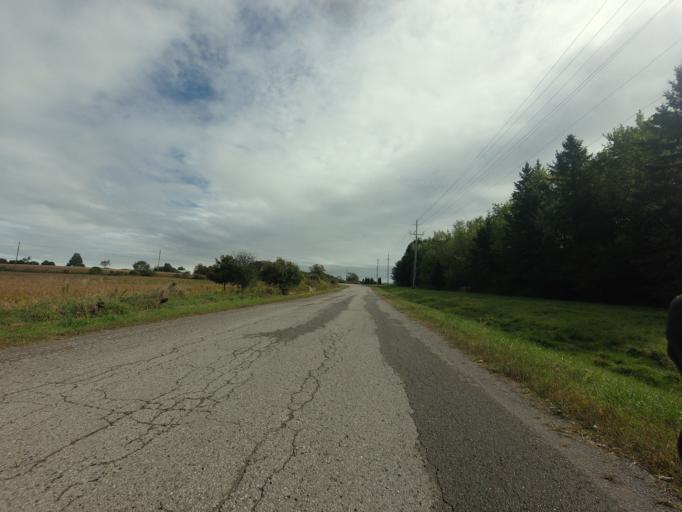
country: CA
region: Ontario
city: Cobourg
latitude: 43.9294
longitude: -78.3874
